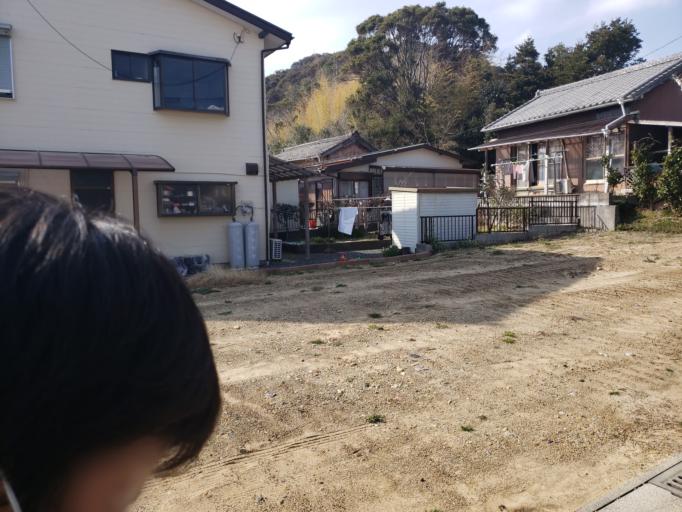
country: JP
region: Shizuoka
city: Kosai-shi
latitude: 34.6800
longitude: 137.5155
